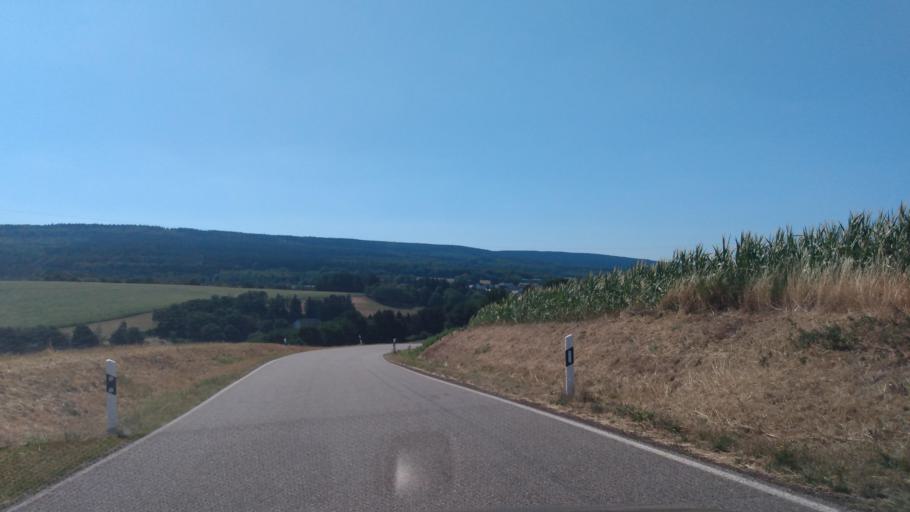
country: DE
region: Rheinland-Pfalz
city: Morbach
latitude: 49.8279
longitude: 7.1510
